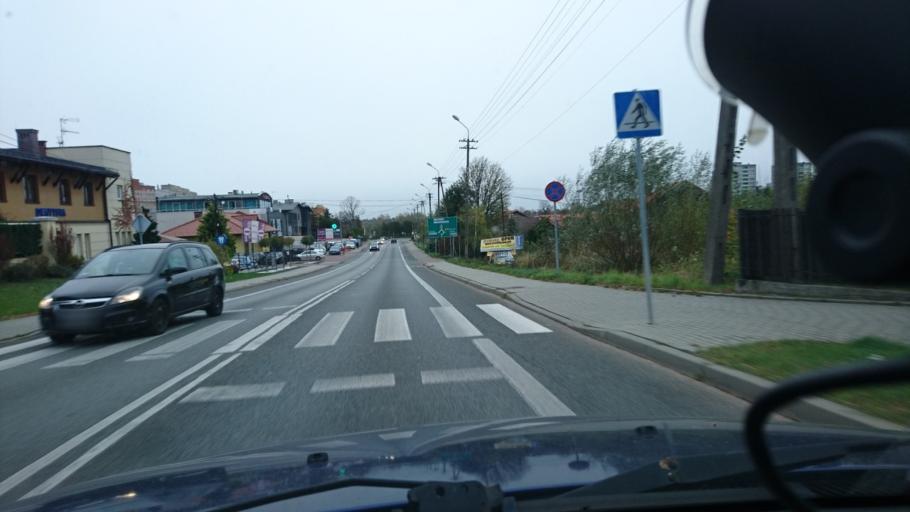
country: PL
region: Silesian Voivodeship
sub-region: Bielsko-Biala
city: Bielsko-Biala
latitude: 49.8109
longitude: 19.0137
